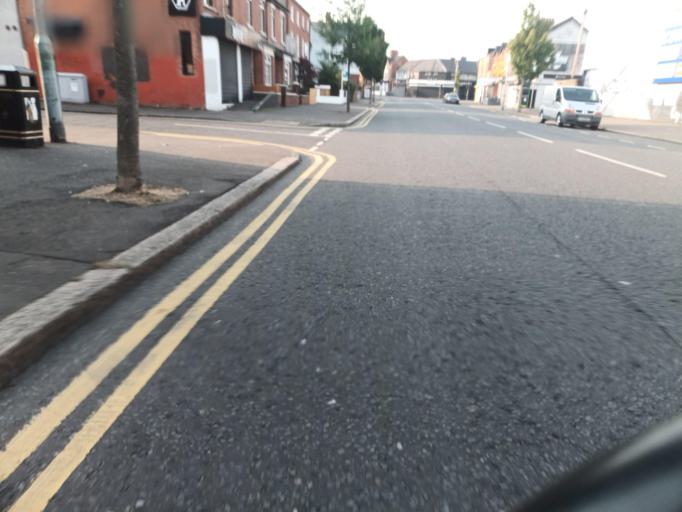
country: GB
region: Northern Ireland
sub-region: Castlereagh District
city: Castlereagh
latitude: 54.5947
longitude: -5.8876
